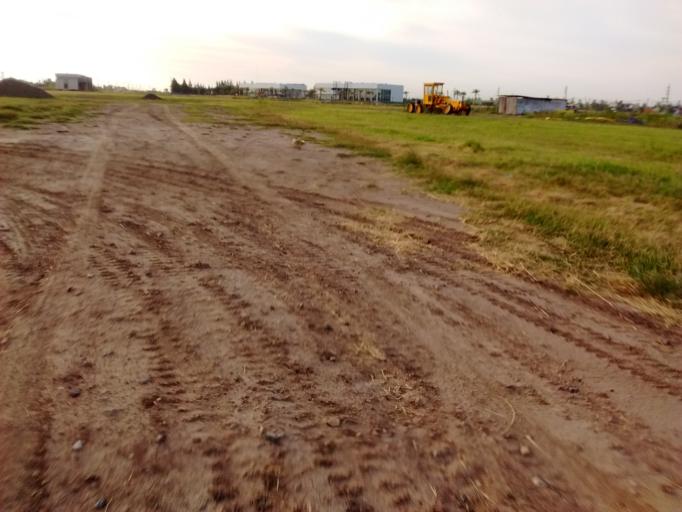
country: AR
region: Santa Fe
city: Roldan
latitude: -32.9419
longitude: -60.8786
